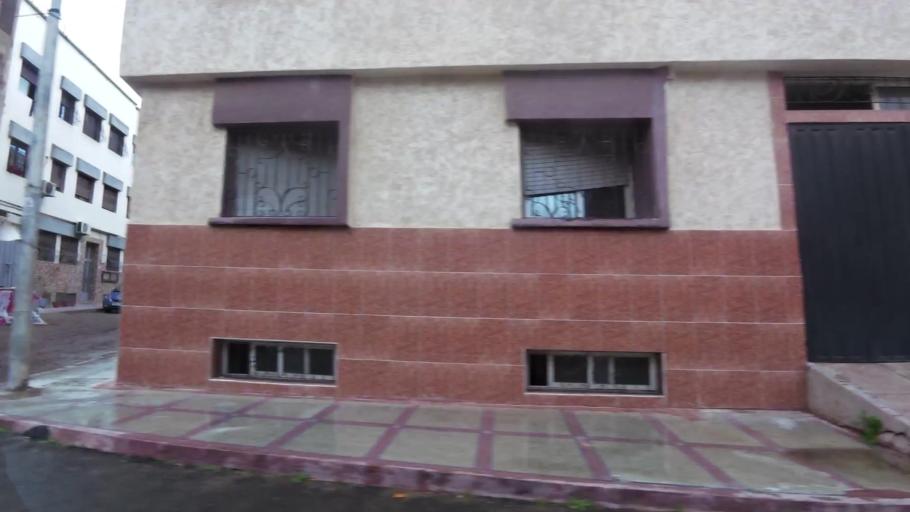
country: MA
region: Grand Casablanca
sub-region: Nouaceur
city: Bouskoura
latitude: 33.5044
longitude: -7.6508
